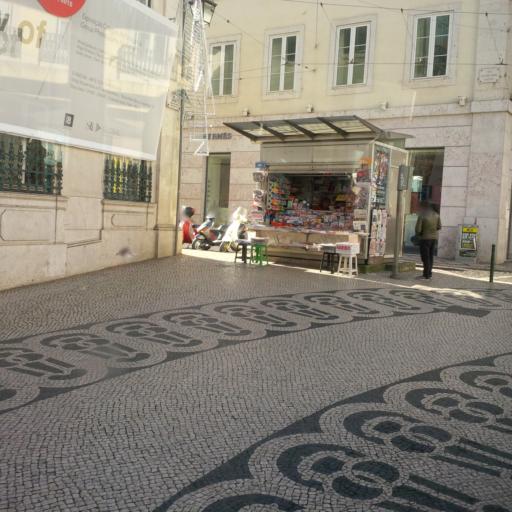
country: PT
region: Lisbon
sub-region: Lisbon
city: Lisbon
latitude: 38.7103
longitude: -9.1422
